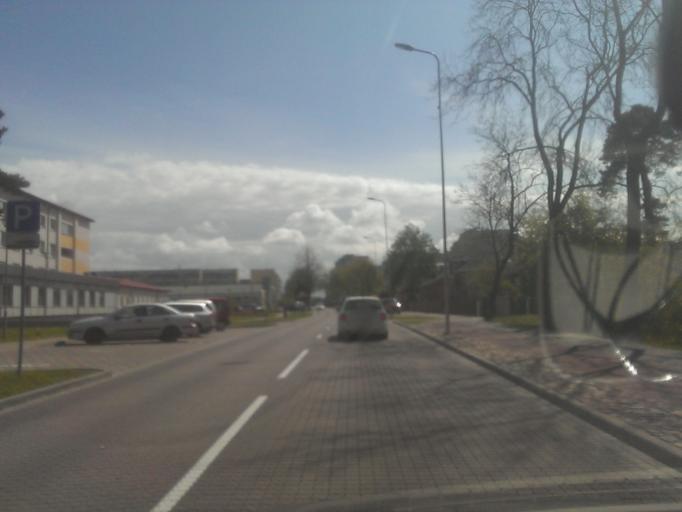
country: LV
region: Ventspils
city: Ventspils
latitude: 57.3870
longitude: 21.5430
